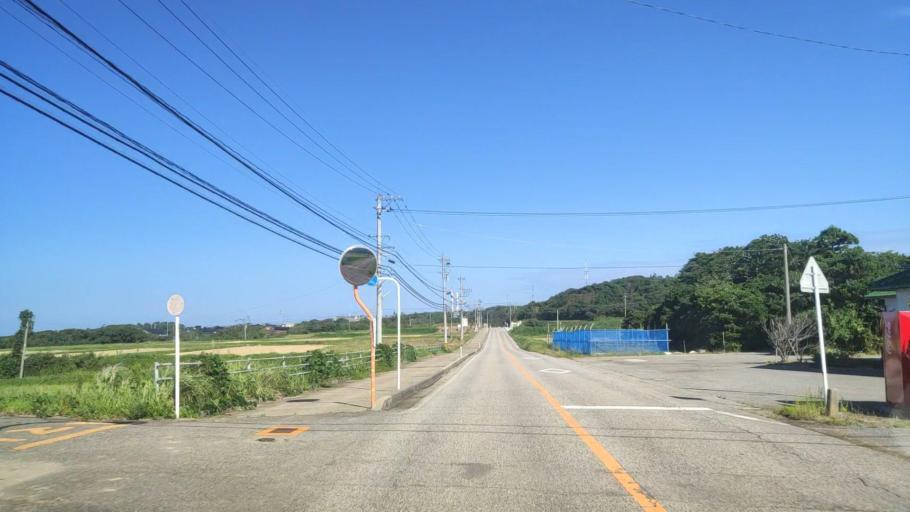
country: JP
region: Ishikawa
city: Hakui
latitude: 37.0460
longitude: 136.7382
